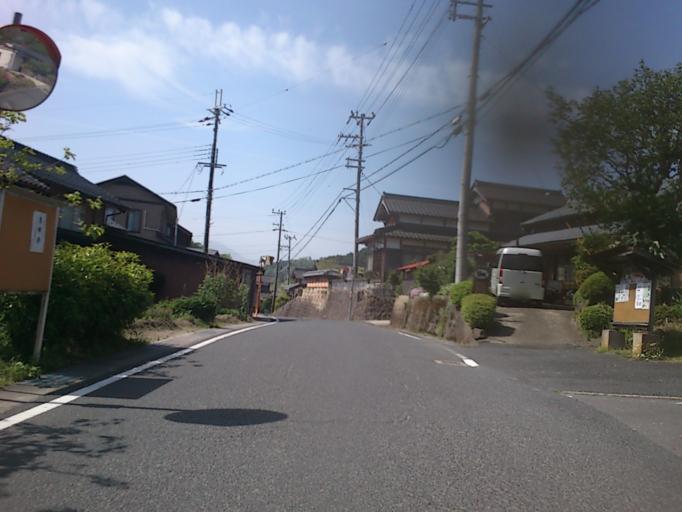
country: JP
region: Kyoto
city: Miyazu
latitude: 35.5634
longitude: 135.1131
